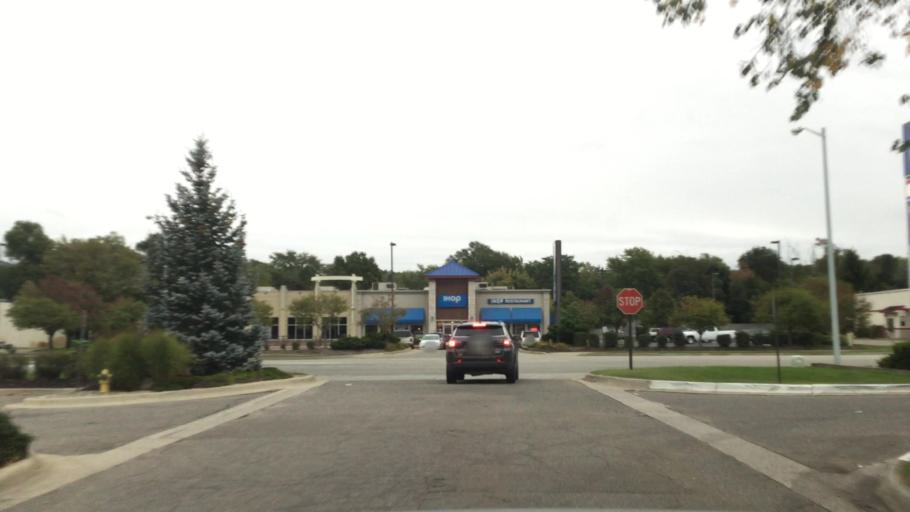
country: US
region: Michigan
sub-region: Kalamazoo County
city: Portage
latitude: 42.2396
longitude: -85.5901
